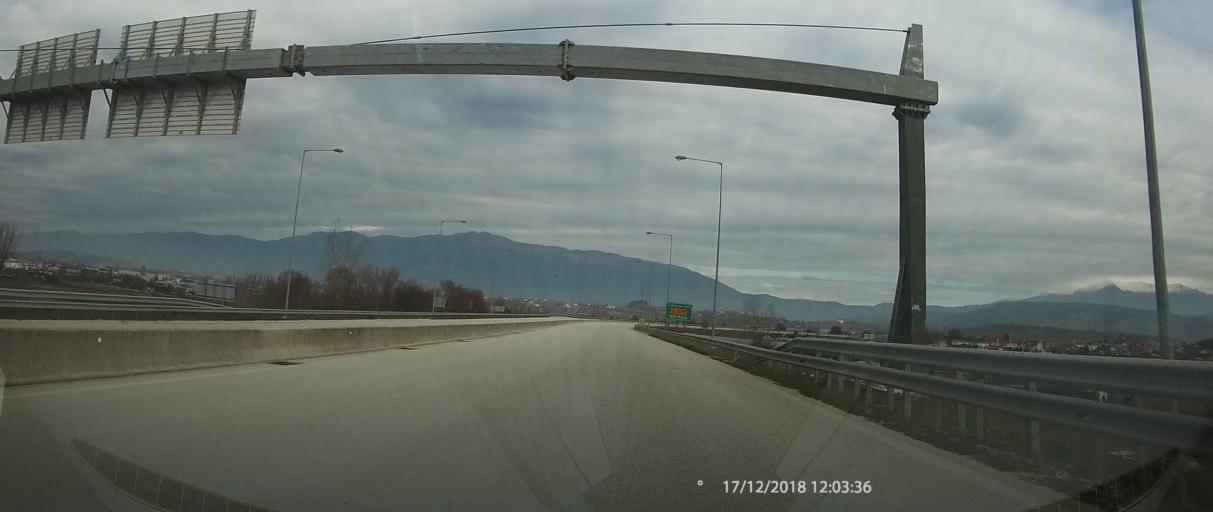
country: GR
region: Epirus
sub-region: Nomos Ioanninon
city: Pedini
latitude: 39.5985
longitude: 20.8653
